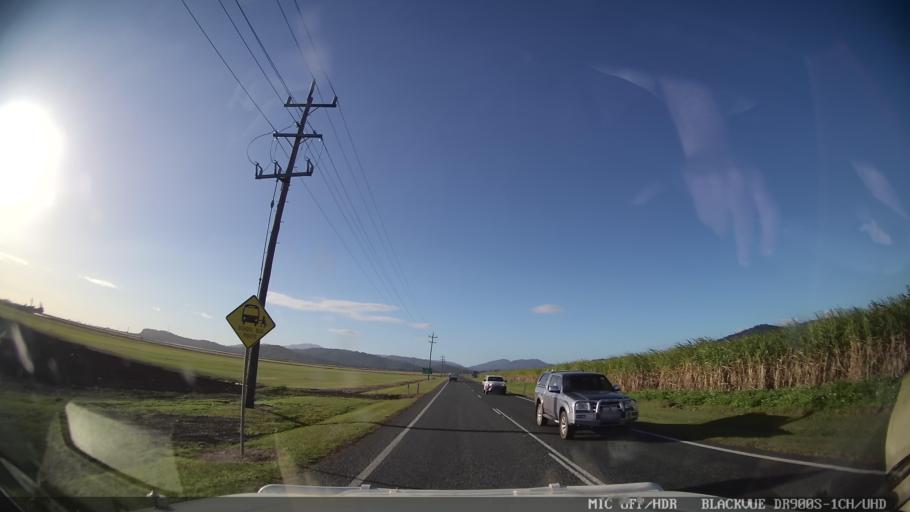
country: AU
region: Queensland
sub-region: Whitsunday
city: Proserpine
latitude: -20.3901
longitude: 148.5865
